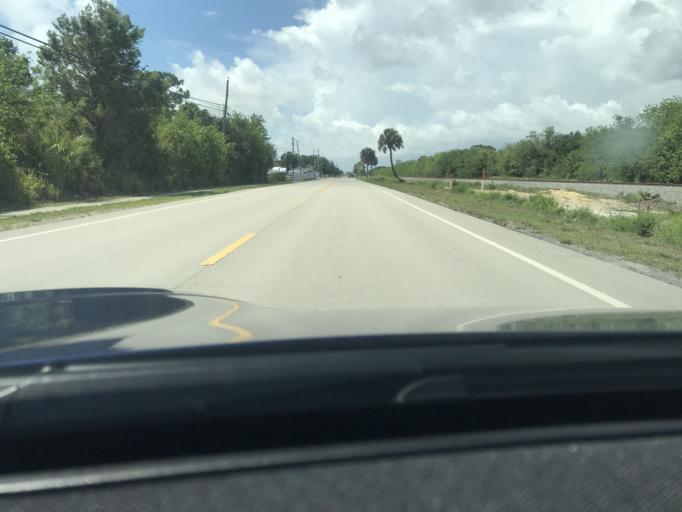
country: US
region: Florida
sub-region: Indian River County
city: Winter Beach
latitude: 27.6984
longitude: -80.4164
